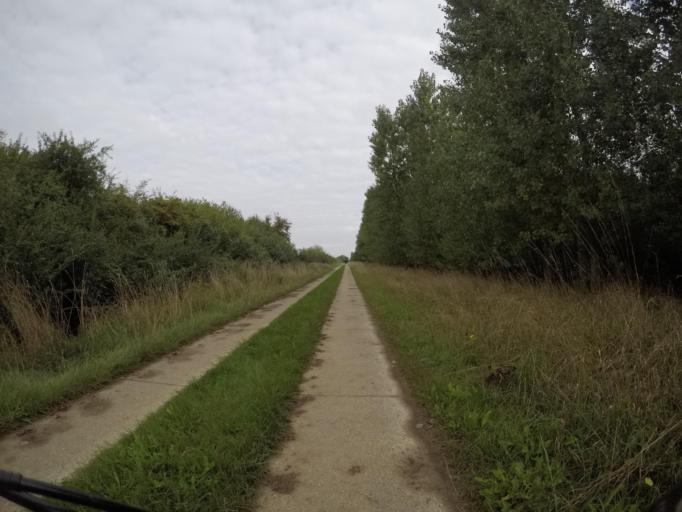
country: DE
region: Lower Saxony
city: Neu Darchau
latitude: 53.3076
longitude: 10.8727
